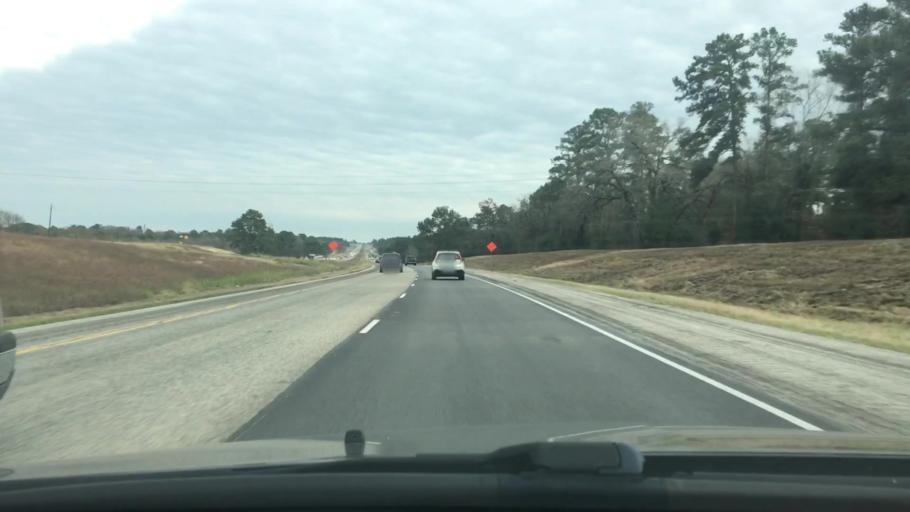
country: US
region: Texas
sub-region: Walker County
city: Huntsville
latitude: 30.7949
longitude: -95.6783
